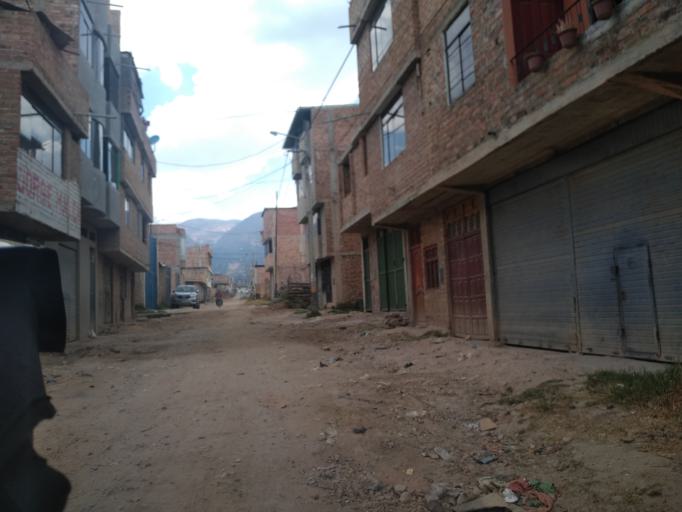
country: PE
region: Cajamarca
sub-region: Provincia de Cajamarca
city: Cajamarca
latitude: -7.1769
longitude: -78.4919
